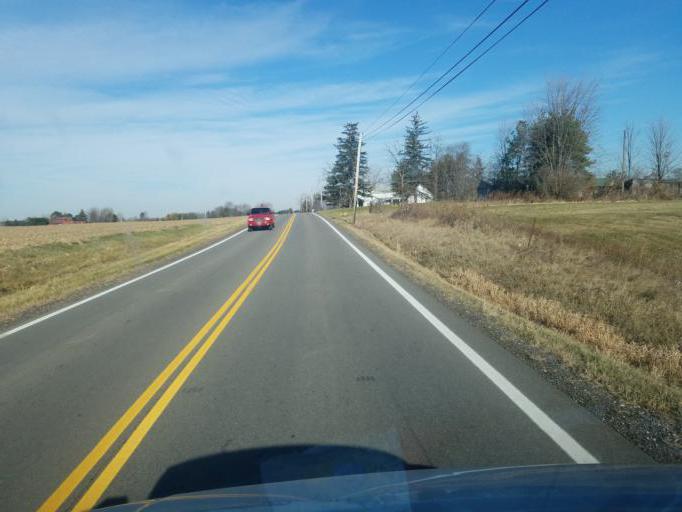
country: US
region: Ohio
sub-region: Richland County
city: Shelby
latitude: 40.8439
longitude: -82.6600
